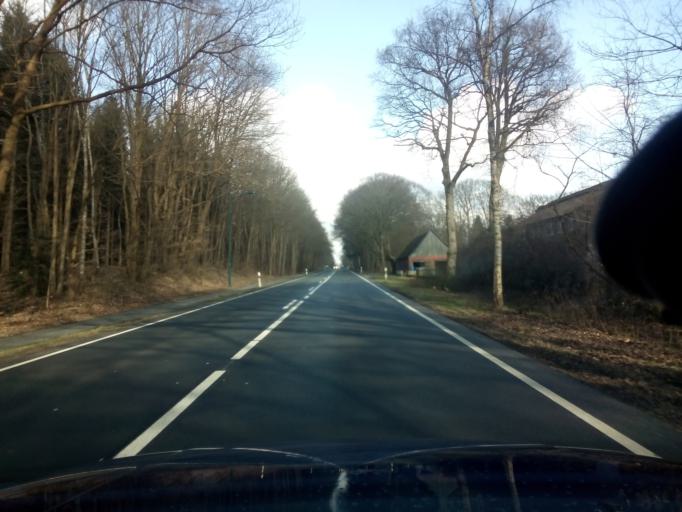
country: DE
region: Lower Saxony
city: Hambergen
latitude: 53.2903
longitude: 8.8300
